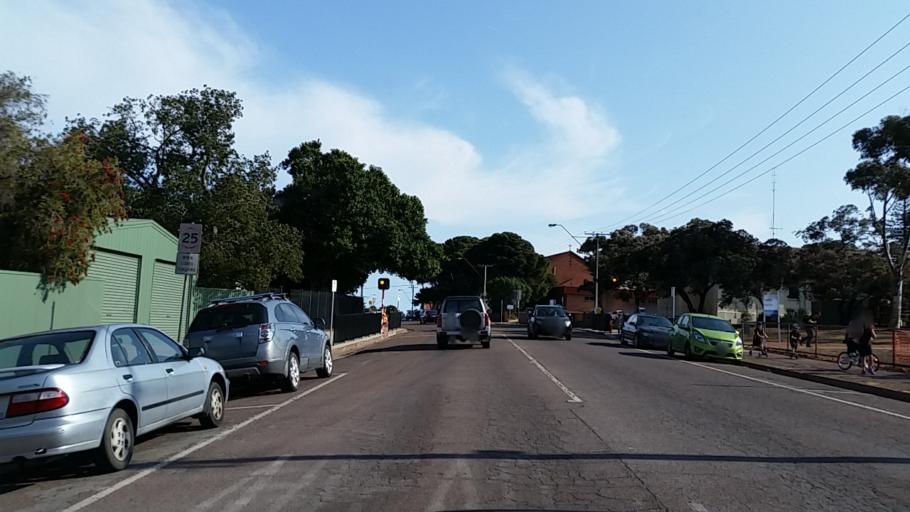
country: AU
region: South Australia
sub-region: Whyalla
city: Whyalla
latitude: -33.0360
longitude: 137.5847
